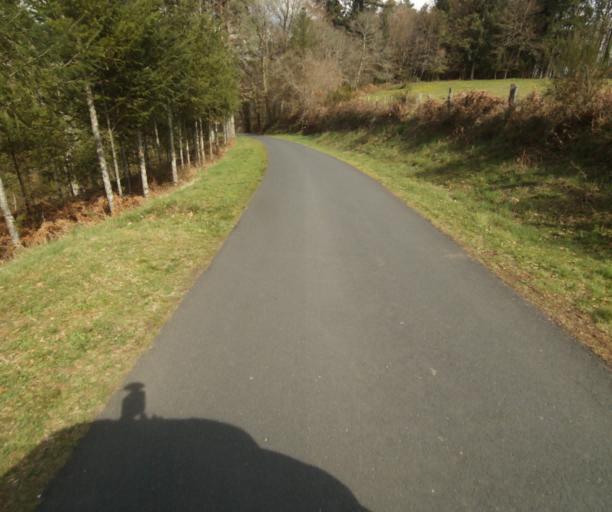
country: FR
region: Limousin
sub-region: Departement de la Correze
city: Correze
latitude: 45.3700
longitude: 1.8873
